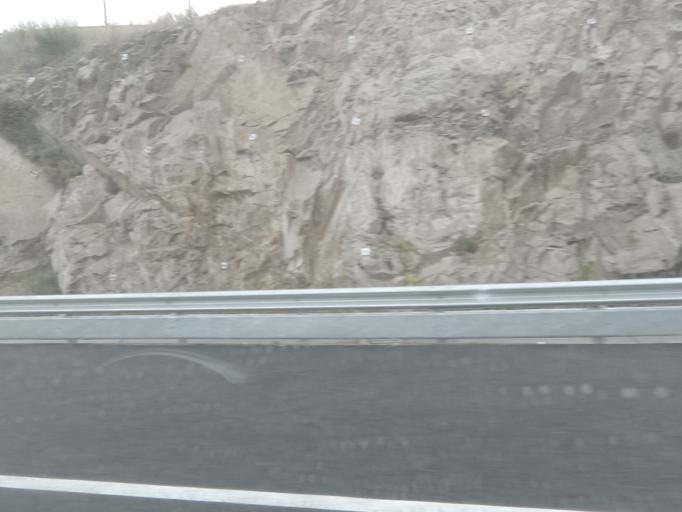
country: PT
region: Porto
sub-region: Maia
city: Pedroucos
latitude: 41.2018
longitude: -8.5808
